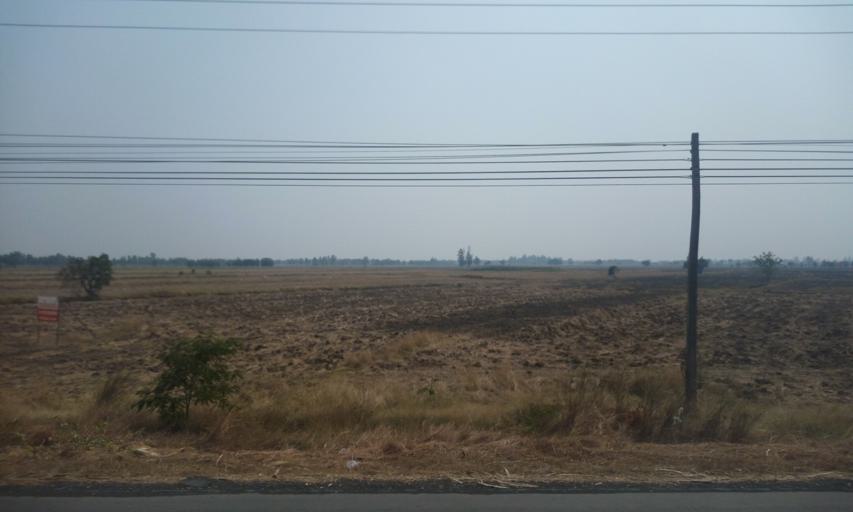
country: TH
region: Nakhon Ratchasima
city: Phimai
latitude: 15.3130
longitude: 102.4293
